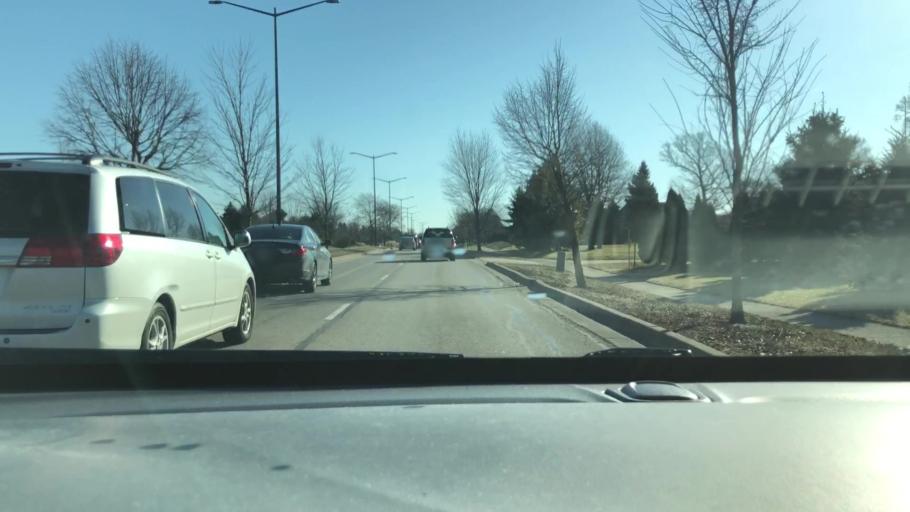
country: US
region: Illinois
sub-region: Kane County
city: Aurora
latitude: 41.7827
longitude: -88.2693
